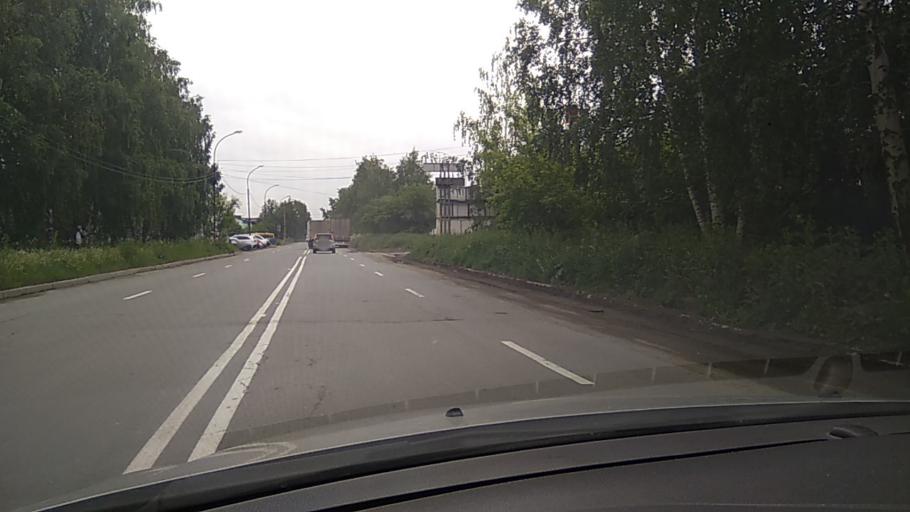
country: RU
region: Sverdlovsk
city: Shuvakish
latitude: 56.8910
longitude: 60.5189
